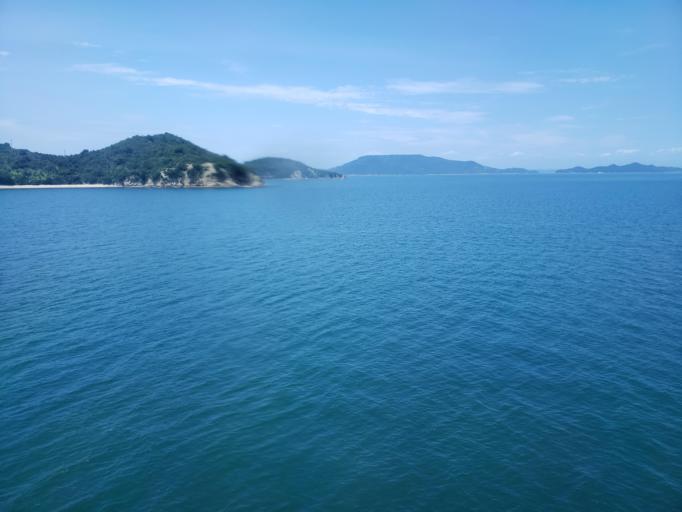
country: JP
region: Kagawa
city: Takamatsu-shi
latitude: 34.4003
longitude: 134.1156
